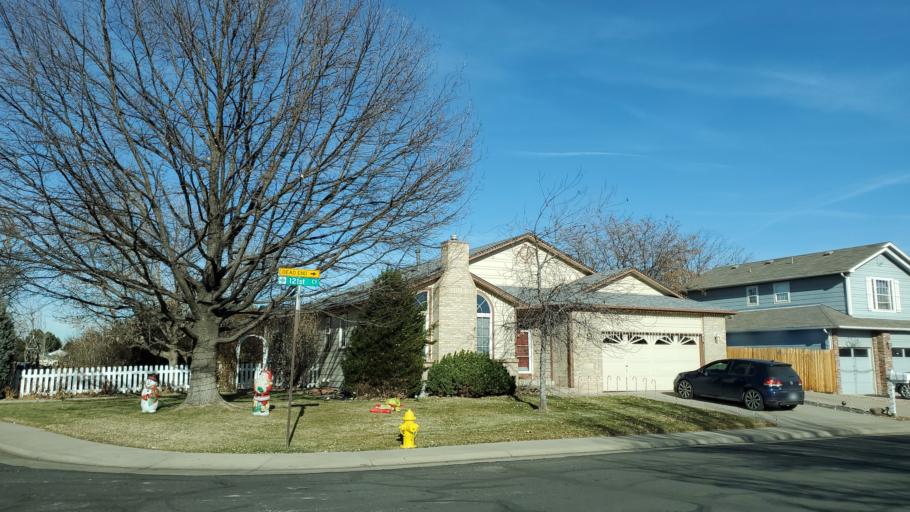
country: US
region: Colorado
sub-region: Adams County
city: Northglenn
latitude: 39.9169
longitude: -104.9520
